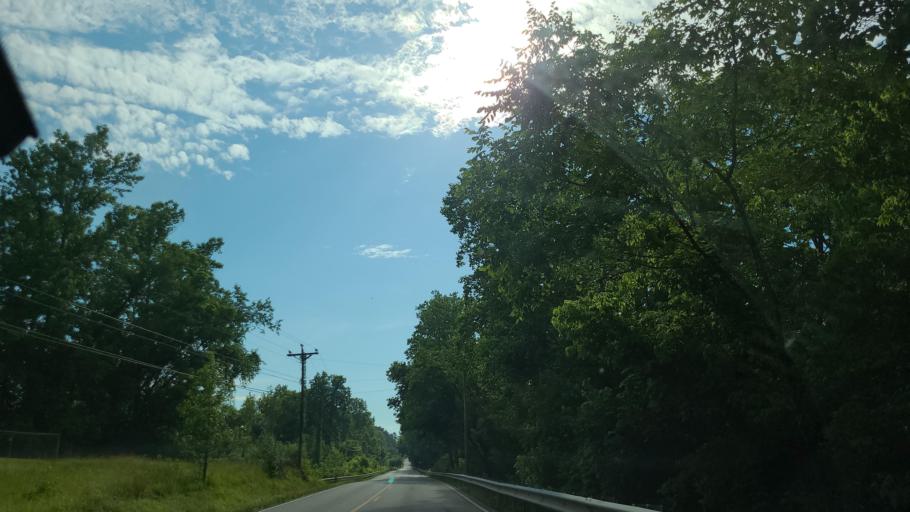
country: US
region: Kentucky
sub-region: Whitley County
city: Williamsburg
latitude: 36.7454
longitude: -84.0476
